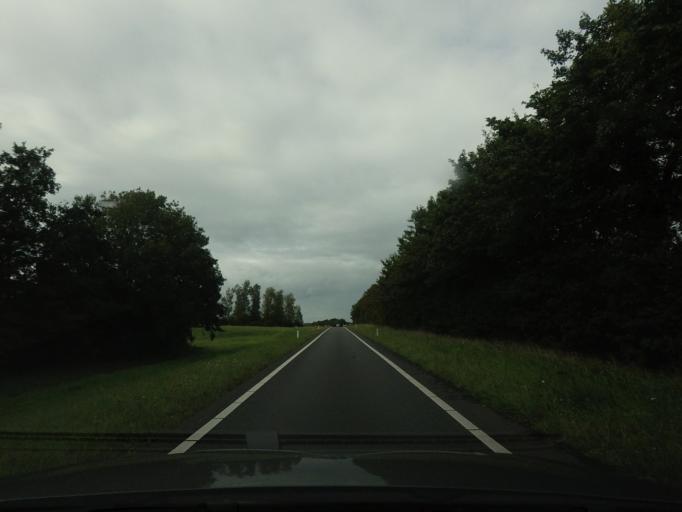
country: NL
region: South Holland
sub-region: Gemeente Noordwijk
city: Noordwijk-Binnen
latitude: 52.2318
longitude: 4.4651
